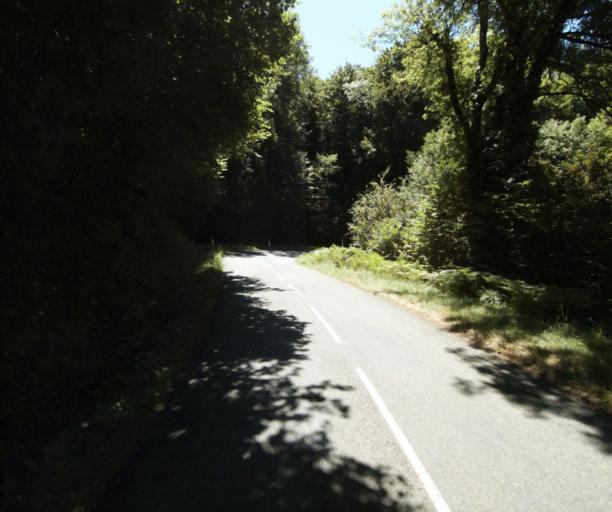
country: FR
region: Midi-Pyrenees
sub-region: Departement du Tarn
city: Dourgne
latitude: 43.4236
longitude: 2.1700
